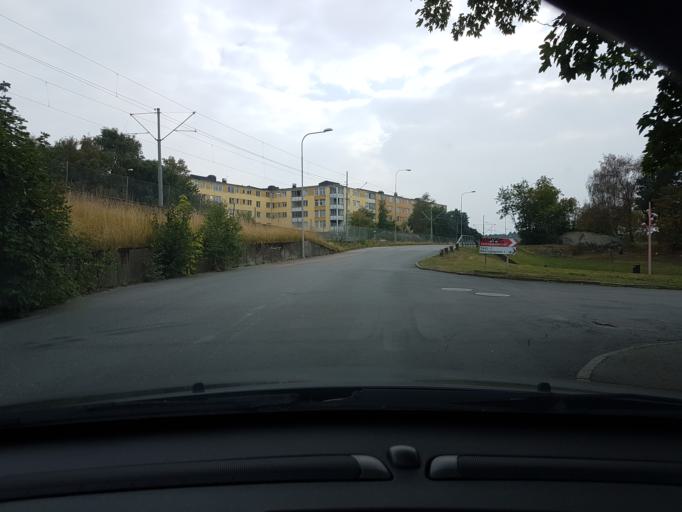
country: SE
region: Vaestra Goetaland
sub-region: Goteborg
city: Majorna
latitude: 57.6471
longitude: 11.9023
